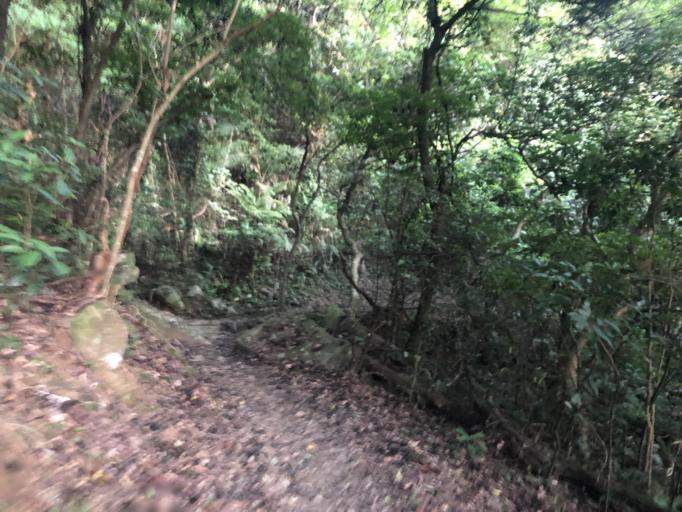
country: HK
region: Tsuen Wan
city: Tsuen Wan
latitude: 22.3996
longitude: 114.0793
